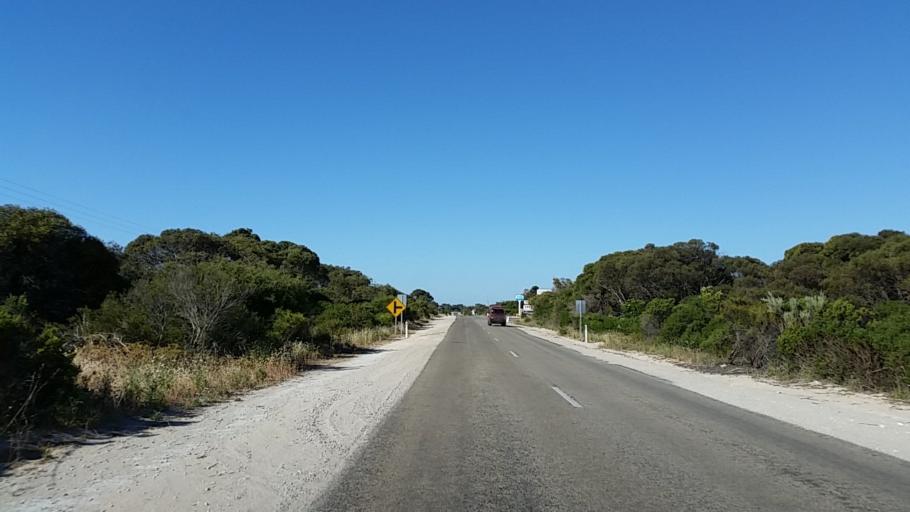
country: AU
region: South Australia
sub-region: Yorke Peninsula
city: Honiton
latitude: -35.2368
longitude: 136.9794
